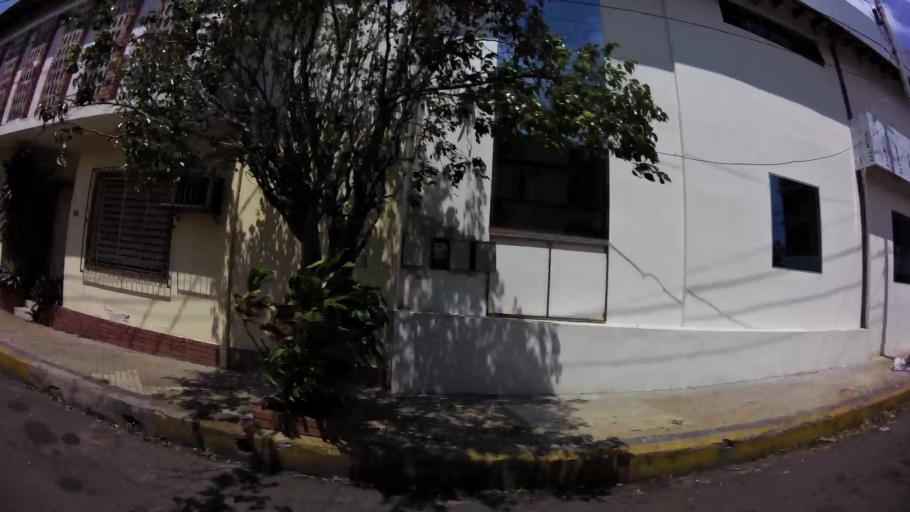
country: PY
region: Asuncion
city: Asuncion
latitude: -25.2922
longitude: -57.6312
